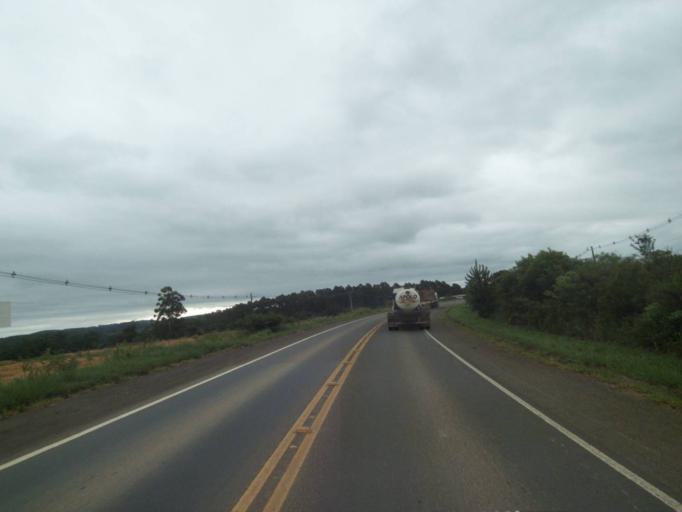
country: BR
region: Parana
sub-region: Telemaco Borba
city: Telemaco Borba
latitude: -24.3874
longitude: -50.6831
